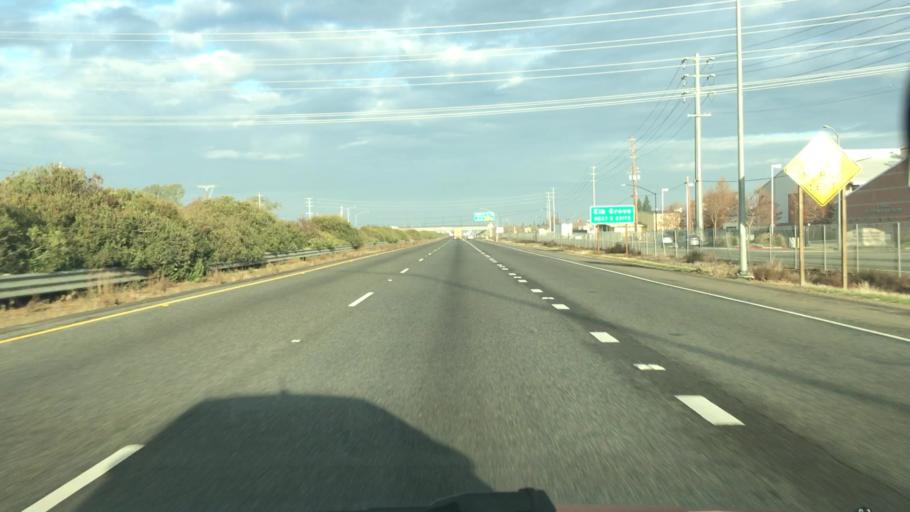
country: US
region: California
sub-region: Sacramento County
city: Elk Grove
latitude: 38.3707
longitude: -121.3561
